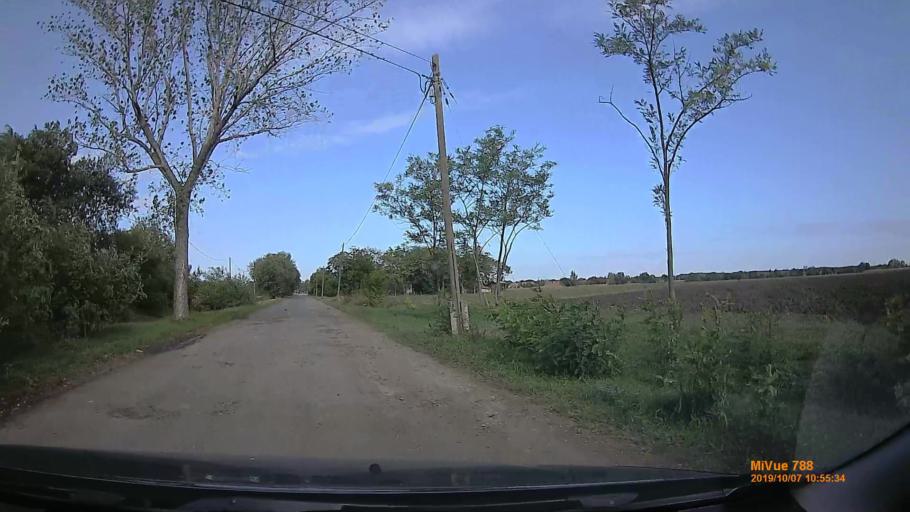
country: HU
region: Bekes
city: Kondoros
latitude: 46.7440
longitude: 20.8044
